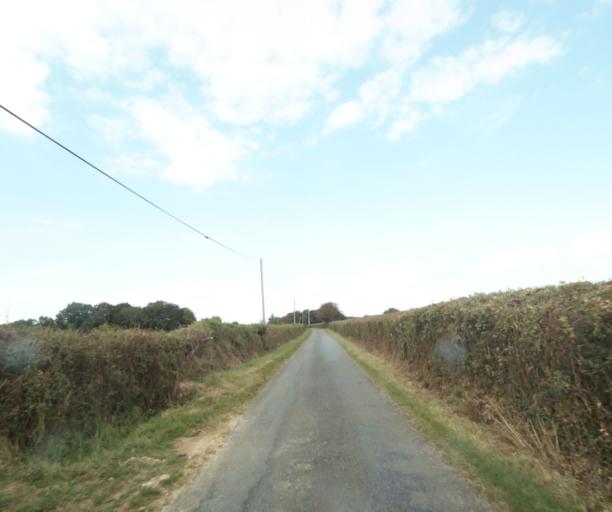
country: FR
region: Bourgogne
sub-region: Departement de Saone-et-Loire
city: Palinges
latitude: 46.5308
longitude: 4.2607
